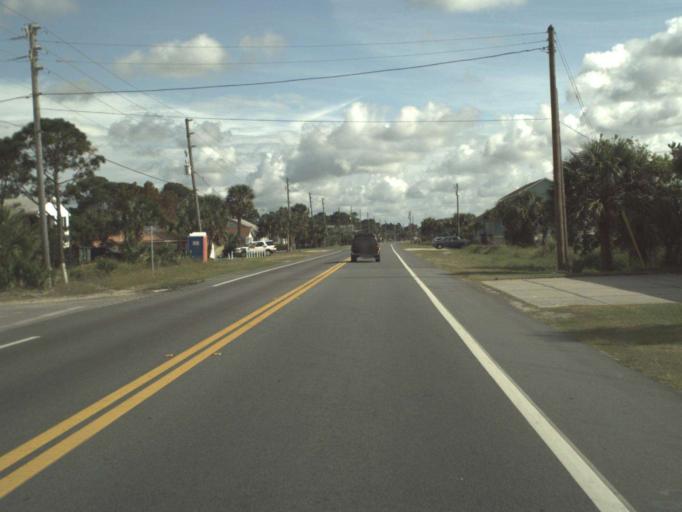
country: US
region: Florida
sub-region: Bay County
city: Mexico Beach
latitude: 29.8997
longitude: -85.3638
